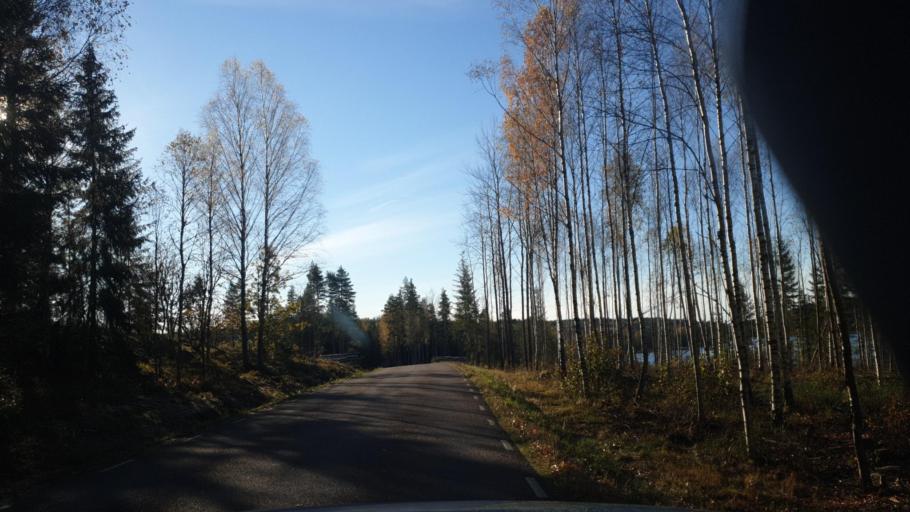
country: SE
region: Vaermland
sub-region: Grums Kommun
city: Grums
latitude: 59.4243
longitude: 13.0867
